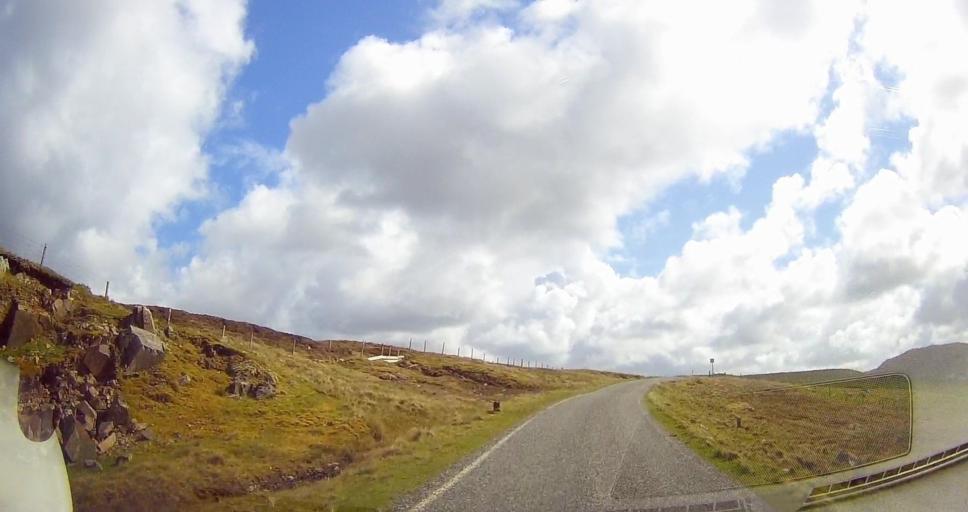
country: GB
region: Scotland
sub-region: Shetland Islands
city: Lerwick
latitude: 60.5631
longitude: -1.3340
